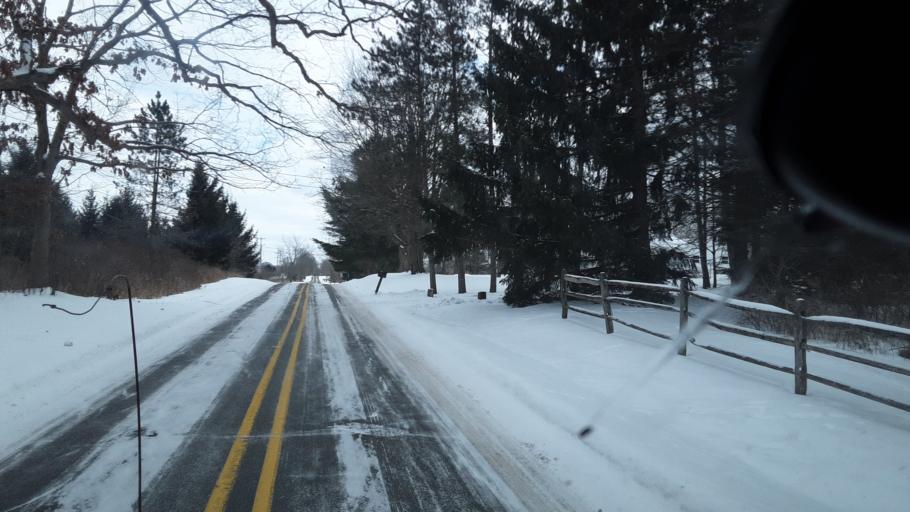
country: US
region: Michigan
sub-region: Ingham County
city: Holt
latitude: 42.6150
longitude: -84.5543
